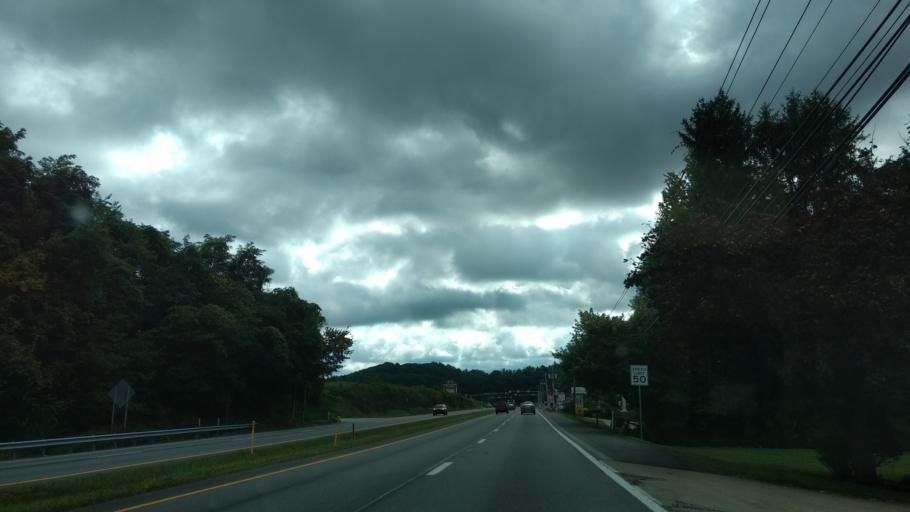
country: US
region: Pennsylvania
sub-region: Westmoreland County
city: Fellsburg
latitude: 40.1858
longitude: -79.8159
